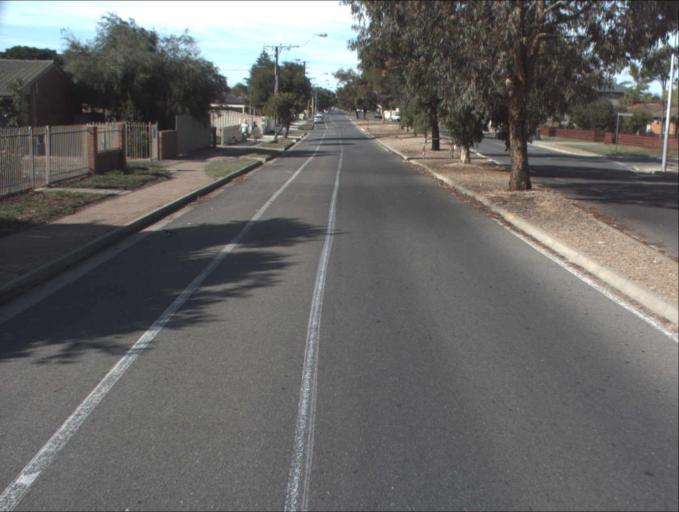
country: AU
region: South Australia
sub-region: Port Adelaide Enfield
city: Birkenhead
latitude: -34.7940
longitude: 138.4967
